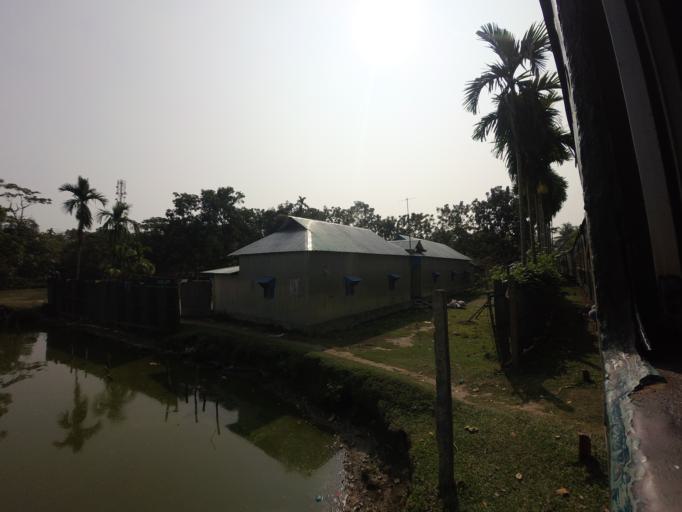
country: BD
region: Dhaka
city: Netrakona
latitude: 25.0083
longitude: 90.6424
